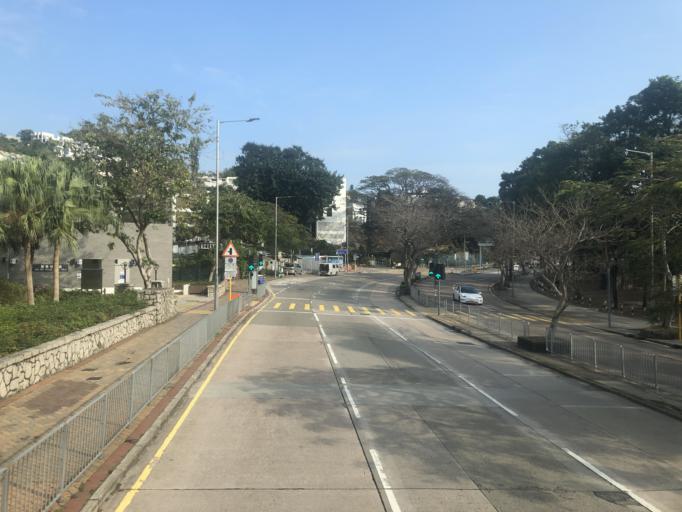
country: HK
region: Wanchai
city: Wan Chai
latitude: 22.2490
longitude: 114.1757
